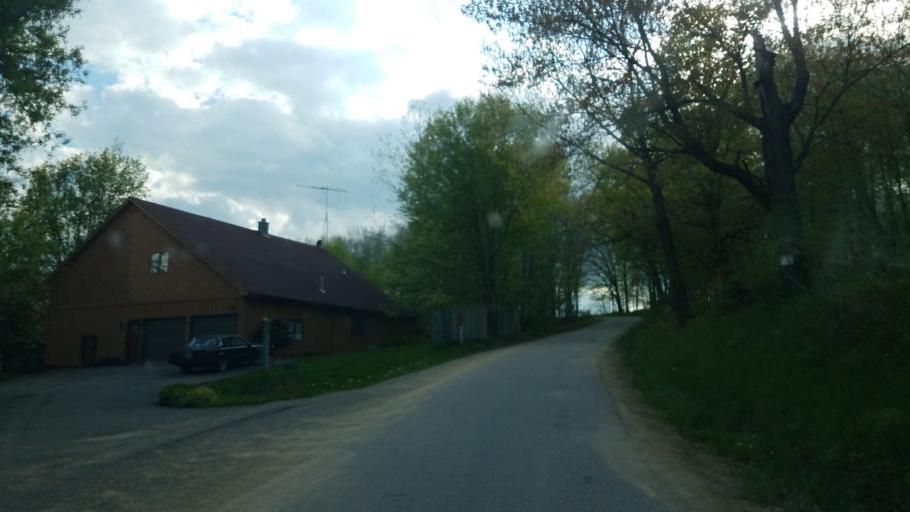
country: US
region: Wisconsin
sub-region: Vernon County
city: Hillsboro
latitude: 43.6543
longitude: -90.3708
